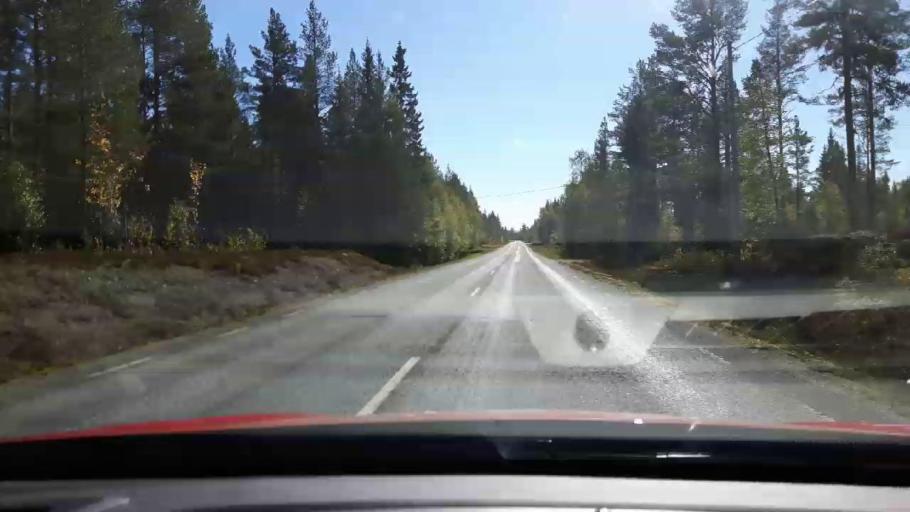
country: SE
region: Jaemtland
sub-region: Harjedalens Kommun
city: Sveg
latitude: 62.3704
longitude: 13.9850
